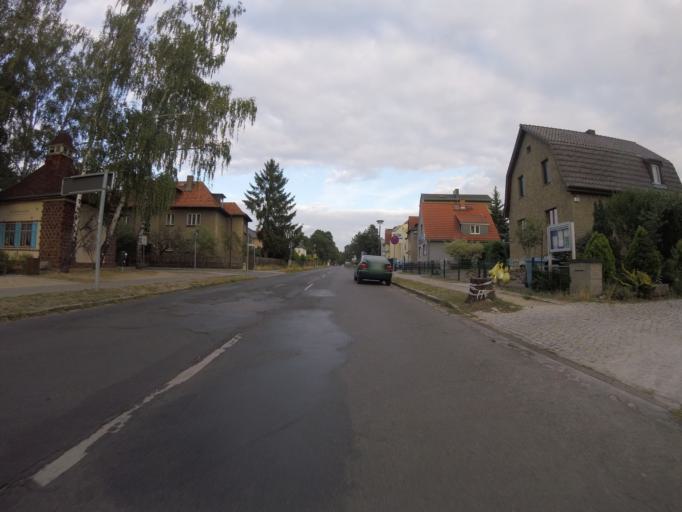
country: DE
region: Brandenburg
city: Birkenwerder
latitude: 52.6869
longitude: 13.2919
